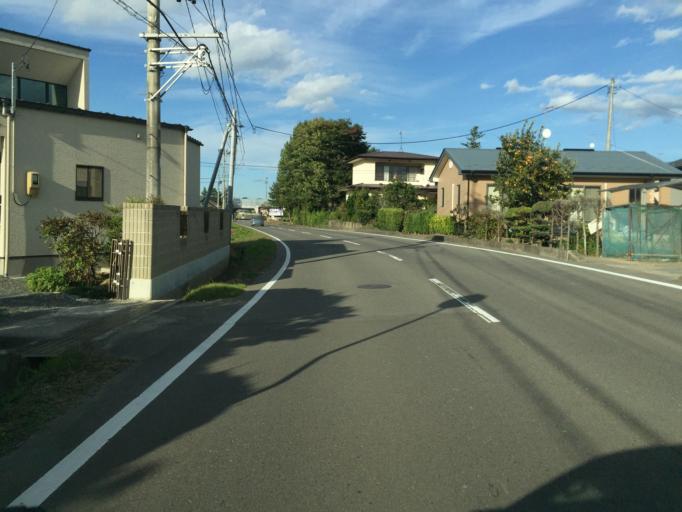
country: JP
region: Fukushima
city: Fukushima-shi
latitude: 37.7133
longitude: 140.4362
